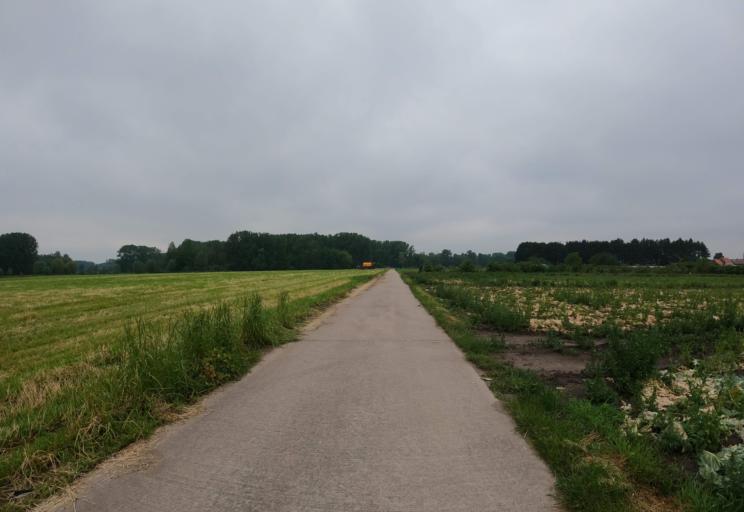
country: BE
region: Flanders
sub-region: Provincie Antwerpen
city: Puurs
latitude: 51.0669
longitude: 4.2737
